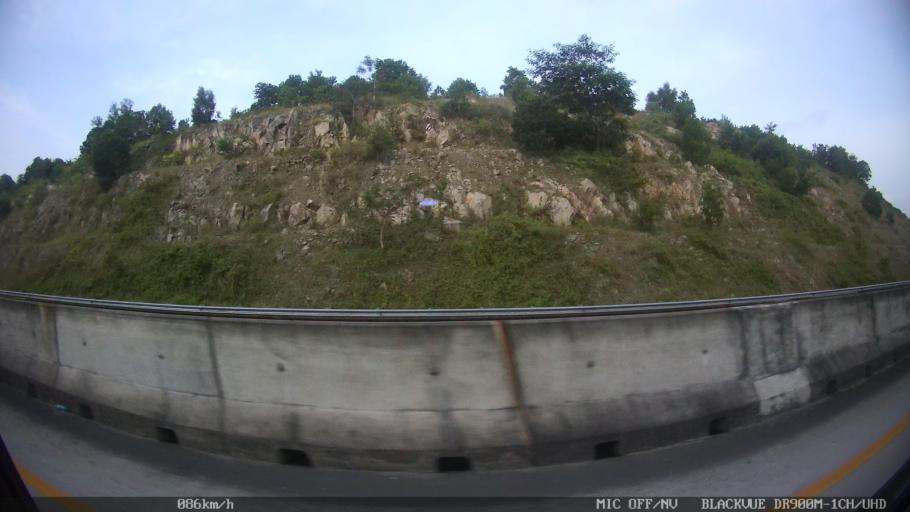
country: ID
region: Lampung
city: Penengahan
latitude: -5.8556
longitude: 105.7297
